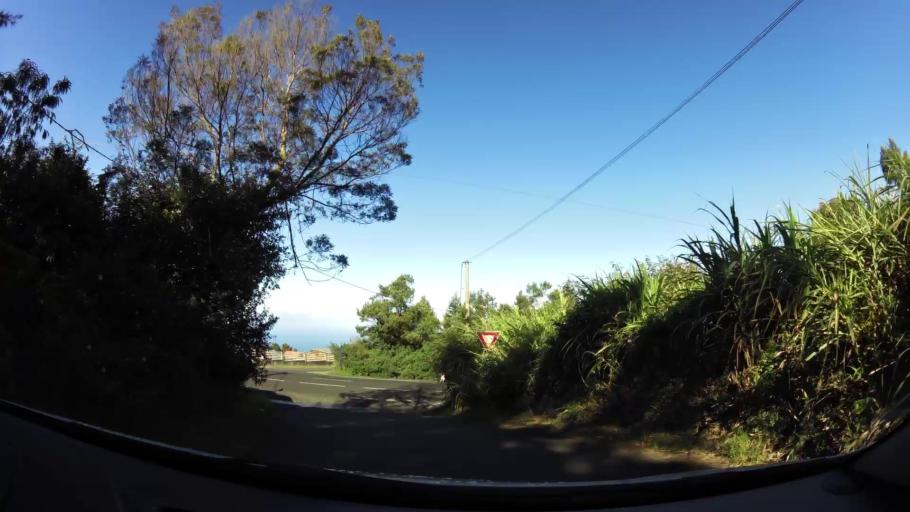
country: RE
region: Reunion
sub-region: Reunion
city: Le Tampon
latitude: -21.2318
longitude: 55.5425
